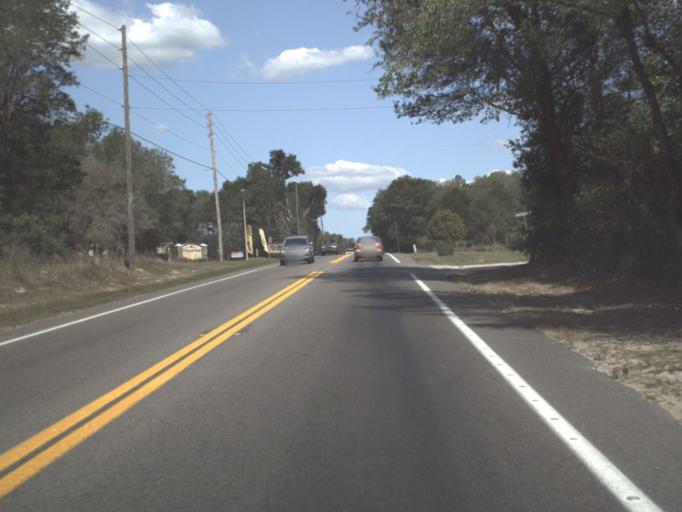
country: US
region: Florida
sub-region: Lake County
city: Mount Plymouth
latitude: 28.8079
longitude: -81.5481
